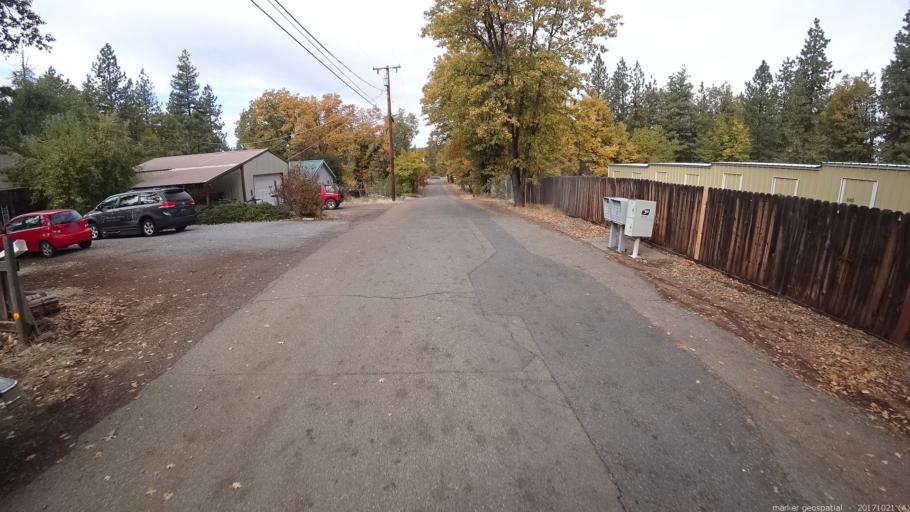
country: US
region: California
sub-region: Shasta County
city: Burney
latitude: 40.9213
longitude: -121.6246
